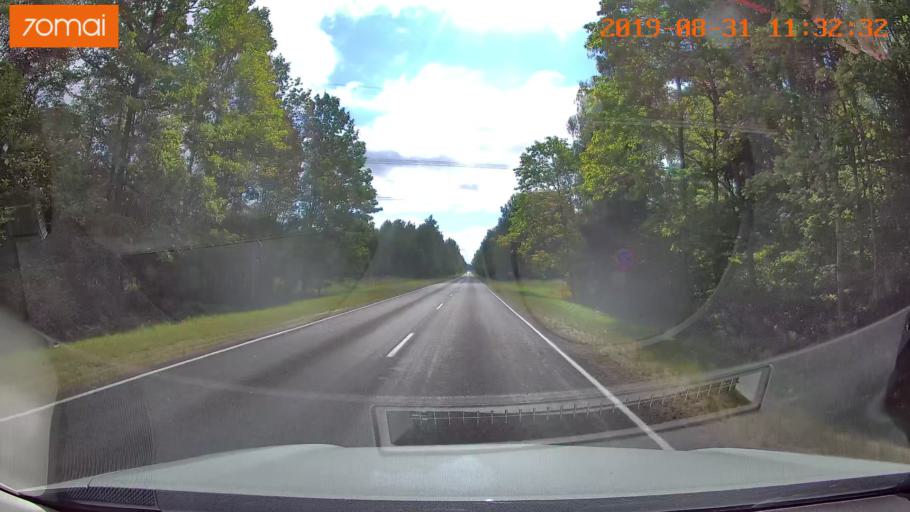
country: BY
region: Mogilev
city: Chavusy
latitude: 53.6922
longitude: 31.1623
